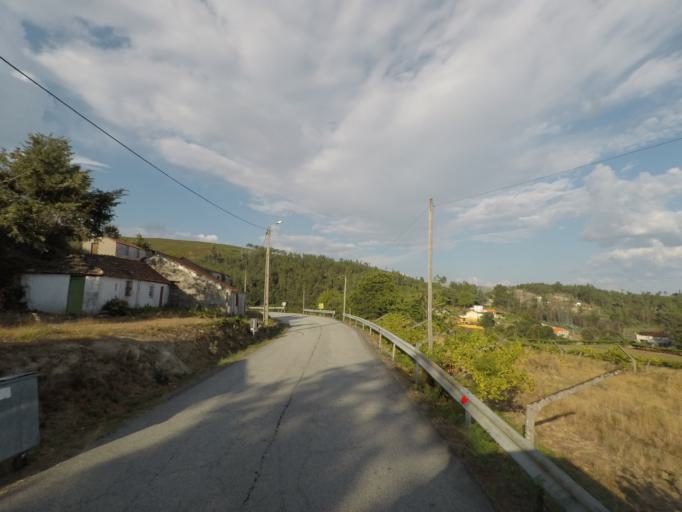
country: PT
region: Porto
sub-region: Baiao
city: Valadares
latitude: 41.1765
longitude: -7.9419
